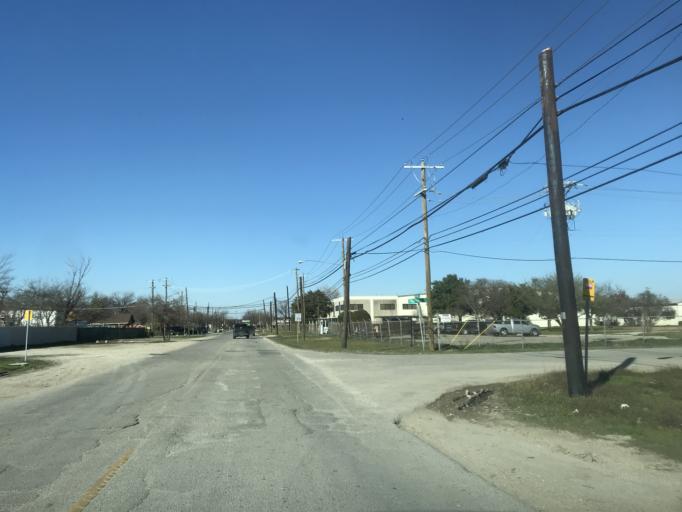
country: US
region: Texas
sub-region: Dallas County
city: Cockrell Hill
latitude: 32.7724
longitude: -96.9037
